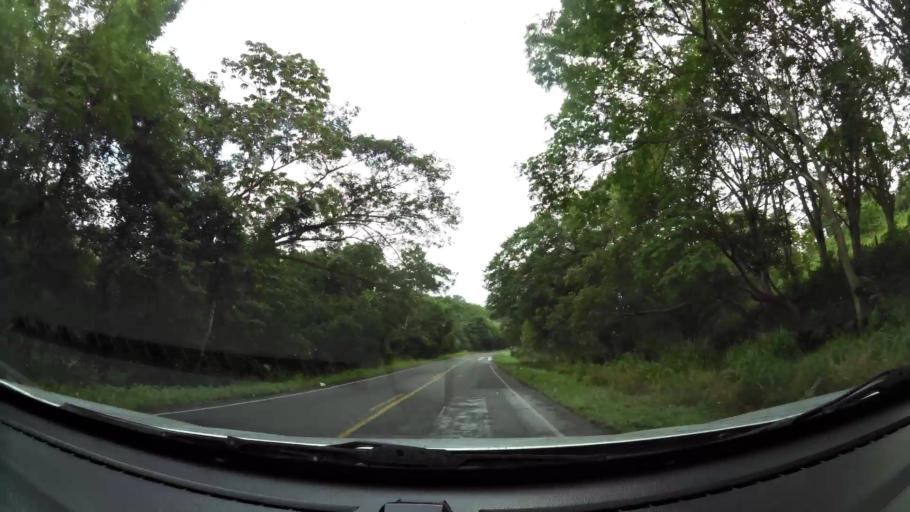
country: CR
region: Guanacaste
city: Juntas
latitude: 10.2358
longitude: -84.9846
